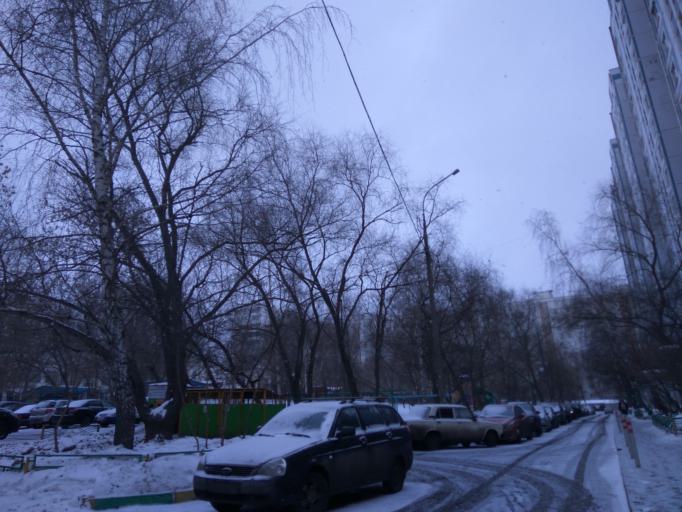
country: RU
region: Moscow
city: Strogino
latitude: 55.7954
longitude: 37.3988
